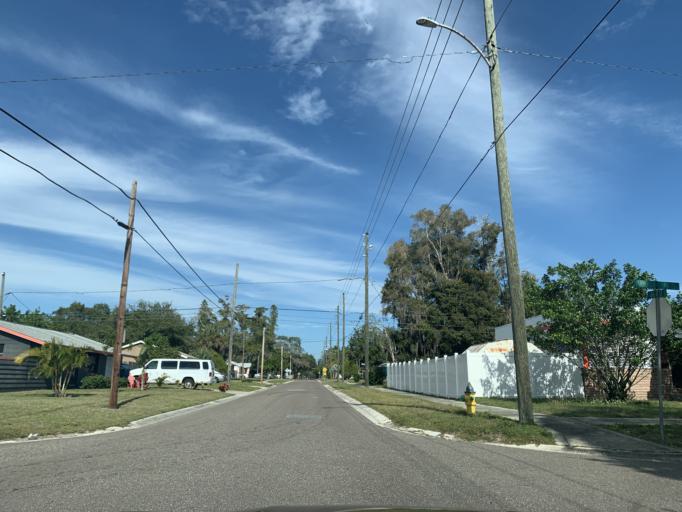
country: US
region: Florida
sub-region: Pinellas County
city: Gulfport
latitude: 27.7461
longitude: -82.6956
